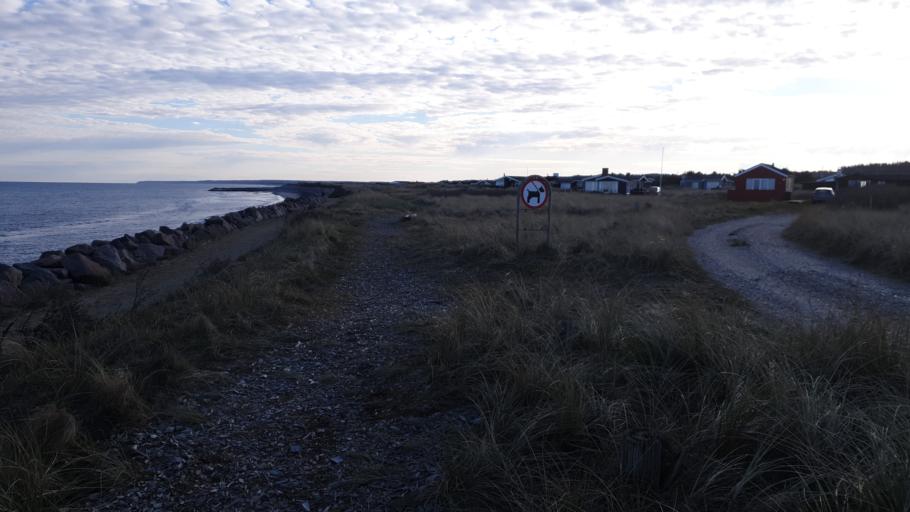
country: DK
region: North Denmark
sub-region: Hjorring Kommune
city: Hjorring
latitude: 57.4872
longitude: 9.8155
